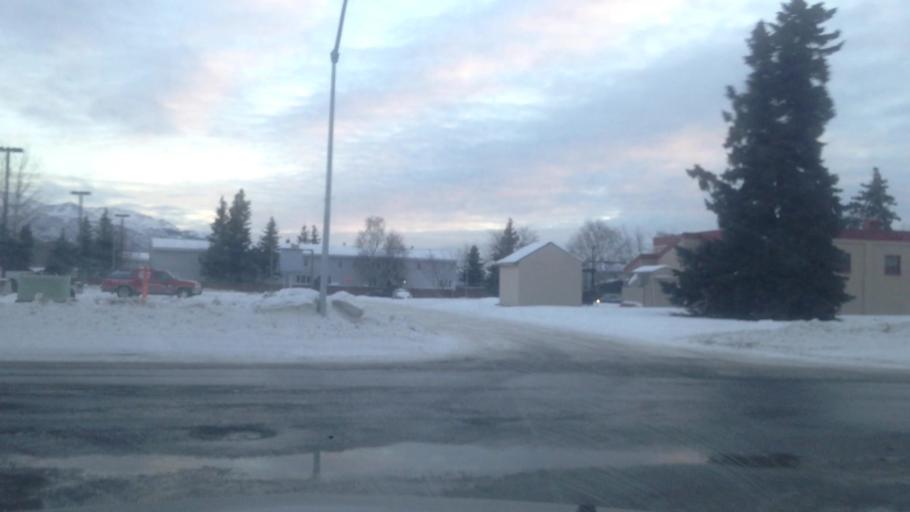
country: US
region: Alaska
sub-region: Anchorage Municipality
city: Elmendorf Air Force Base
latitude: 61.2547
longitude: -149.6862
